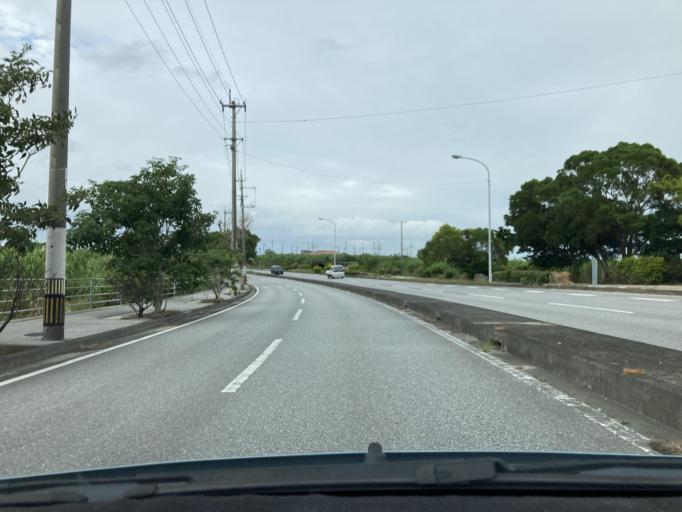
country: JP
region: Okinawa
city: Tomigusuku
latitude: 26.1585
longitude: 127.7022
